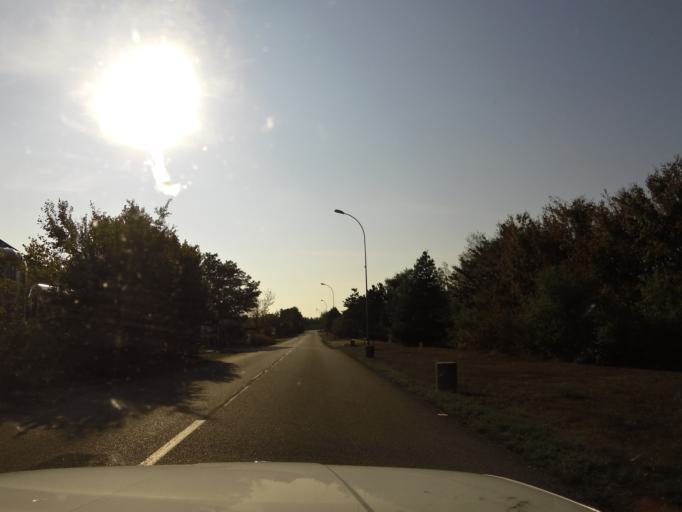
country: FR
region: Rhone-Alpes
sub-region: Departement de l'Ain
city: Saint-Jean-de-Niost
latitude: 45.8377
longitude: 5.2638
